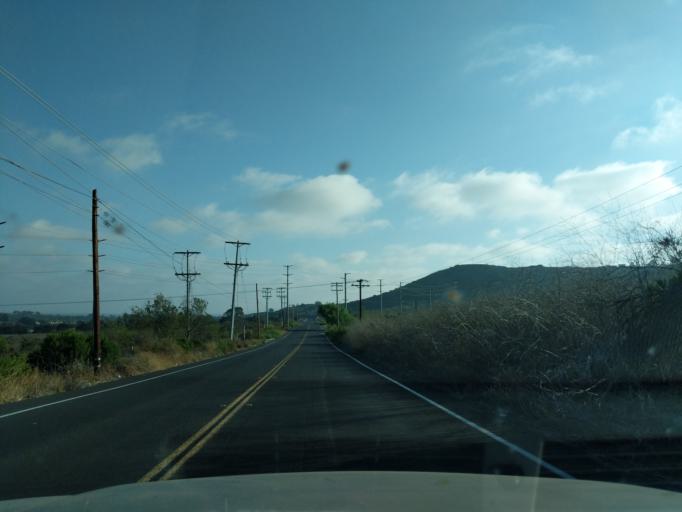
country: US
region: California
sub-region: Orange County
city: San Clemente
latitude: 33.4121
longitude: -117.5829
